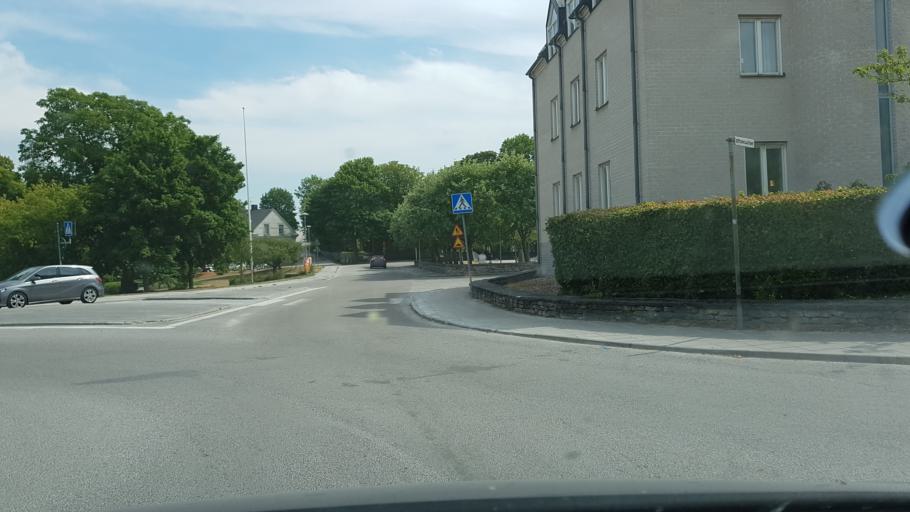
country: SE
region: Gotland
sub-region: Gotland
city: Slite
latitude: 57.7058
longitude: 18.8054
